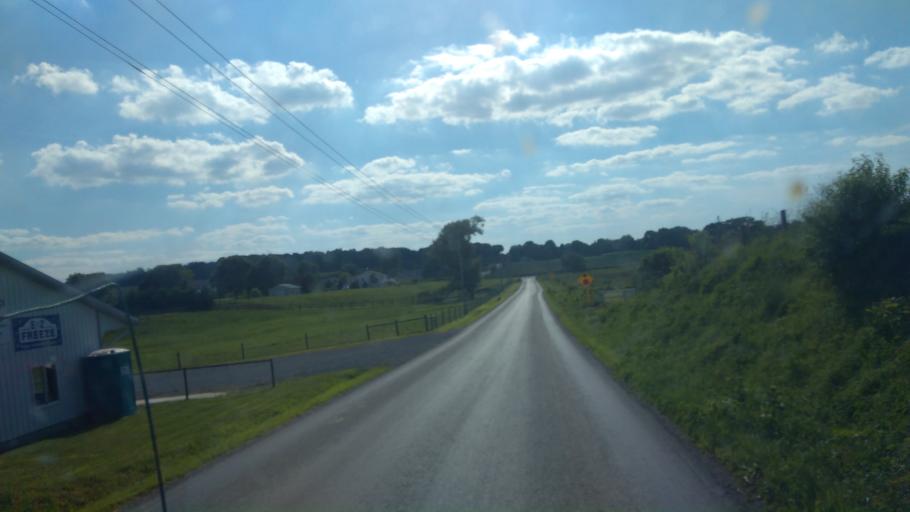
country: US
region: Ohio
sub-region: Wayne County
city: Apple Creek
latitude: 40.7262
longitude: -81.8732
